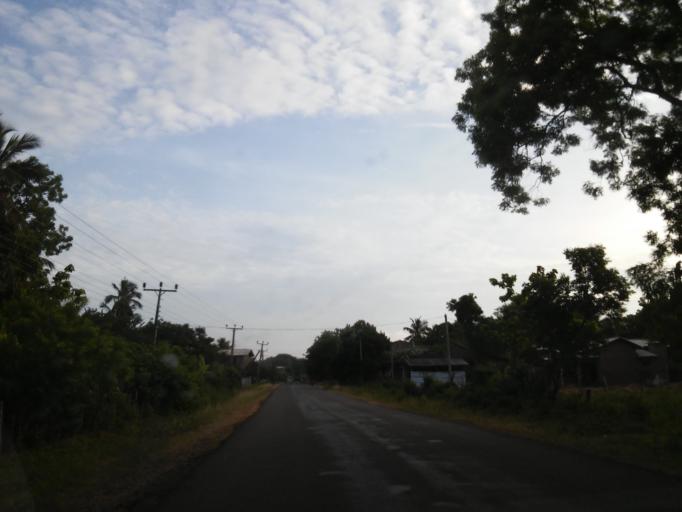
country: LK
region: Central
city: Sigiriya
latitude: 8.1202
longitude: 80.6328
